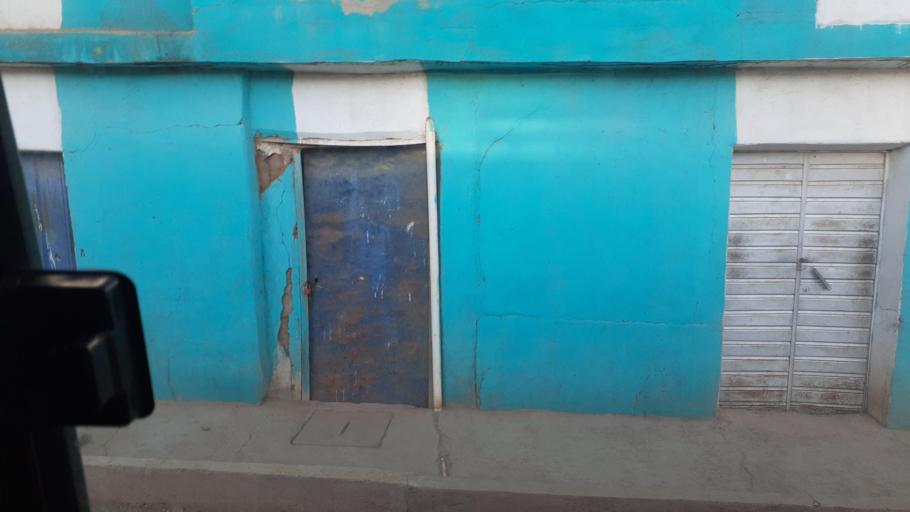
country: BO
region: La Paz
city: Tiahuanaco
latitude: -16.9374
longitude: -68.7647
